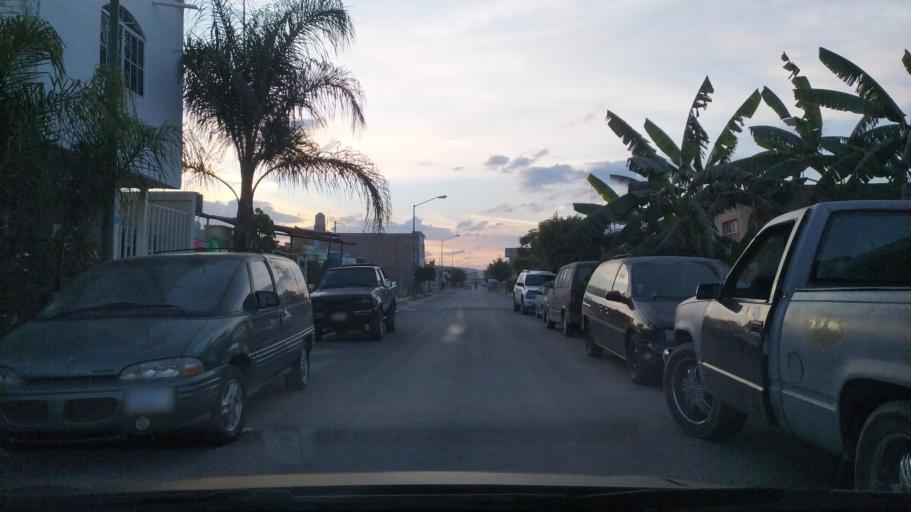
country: MX
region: Guanajuato
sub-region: San Francisco del Rincon
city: Estacion de San Francisco
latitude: 21.0400
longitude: -101.8417
